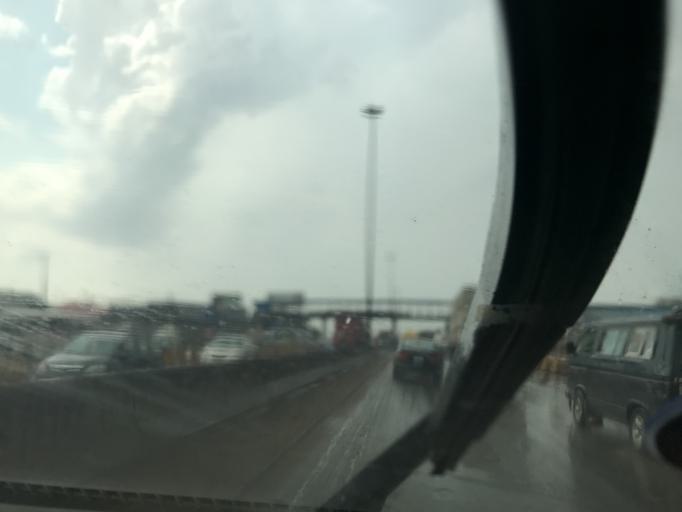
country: NG
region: Lagos
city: Oshodi
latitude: 6.5520
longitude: 3.3429
